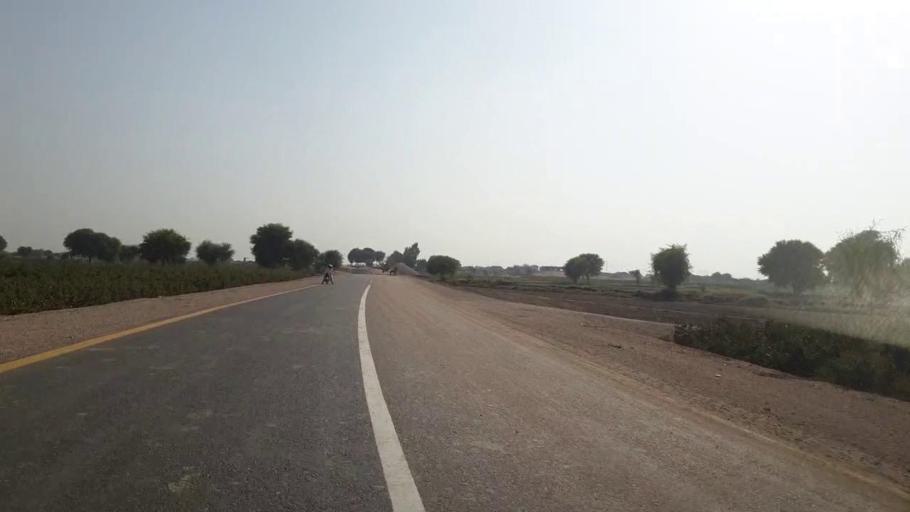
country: PK
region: Sindh
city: Bhan
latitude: 26.5046
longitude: 67.7830
